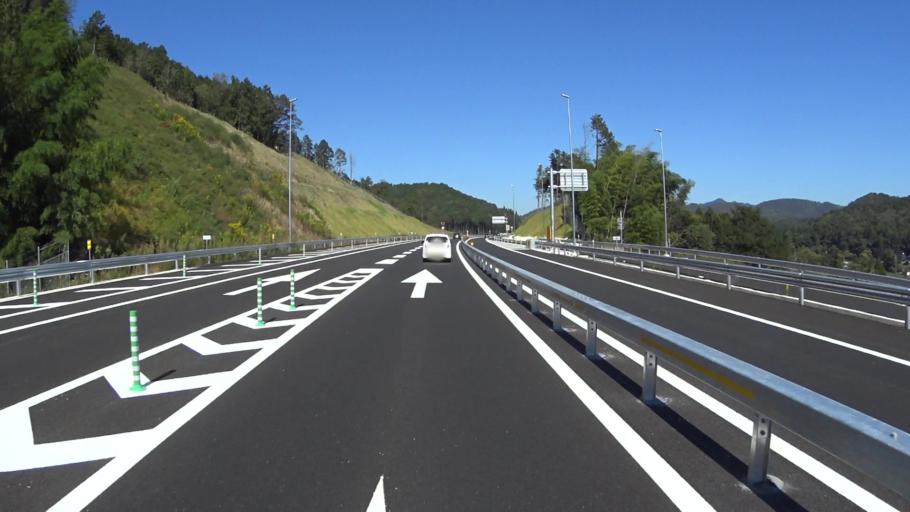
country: JP
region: Kyoto
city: Ayabe
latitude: 35.1868
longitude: 135.3603
